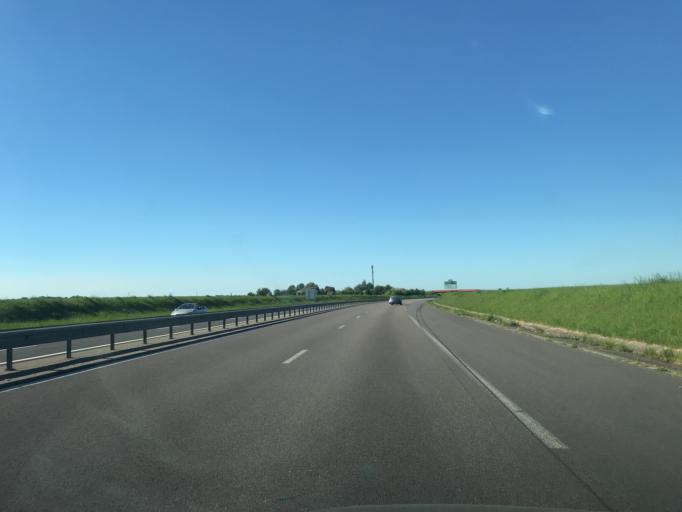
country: FR
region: Haute-Normandie
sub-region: Departement de l'Eure
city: Evreux
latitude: 48.9600
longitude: 1.1985
